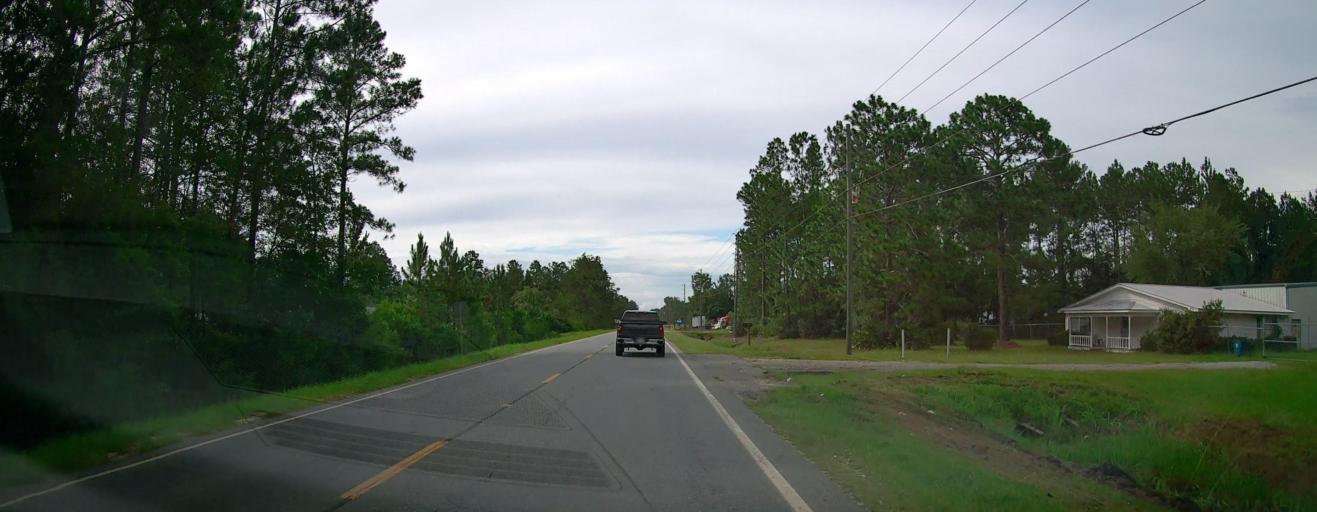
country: US
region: Georgia
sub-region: Wayne County
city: Jesup
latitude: 31.6384
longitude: -81.9045
